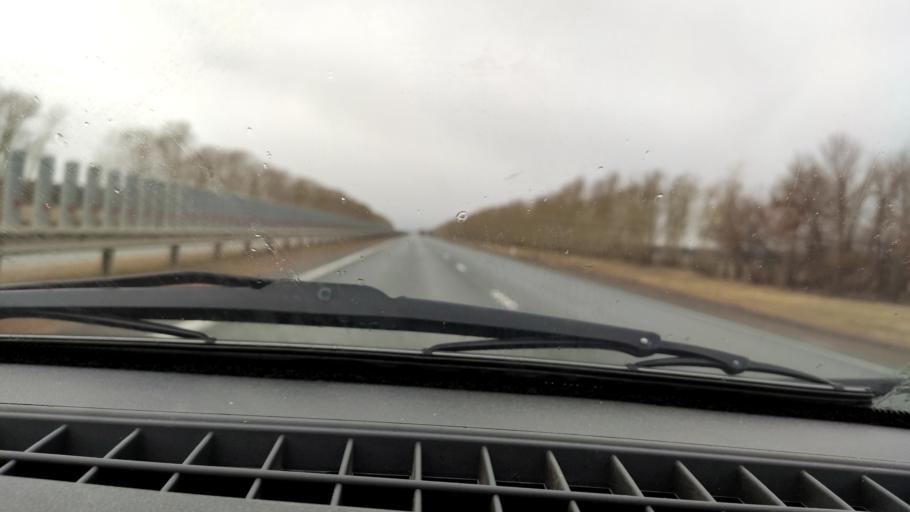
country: RU
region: Bashkortostan
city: Kushnarenkovo
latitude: 55.0341
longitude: 55.4591
